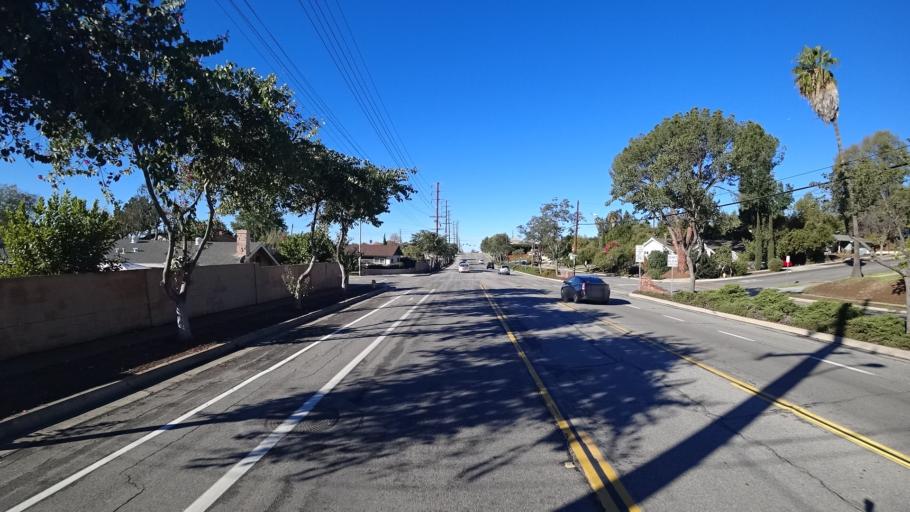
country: US
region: California
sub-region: Orange County
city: La Habra
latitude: 33.9391
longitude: -117.9297
